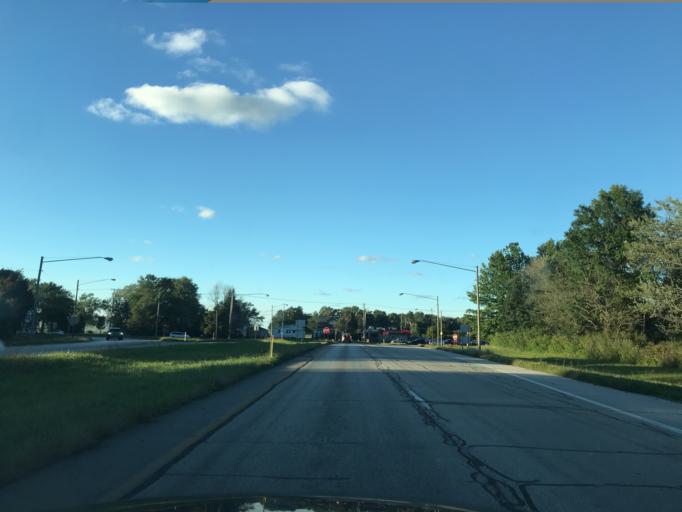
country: US
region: Ohio
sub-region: Ashtabula County
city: Edgewood
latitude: 41.8993
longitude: -80.7821
